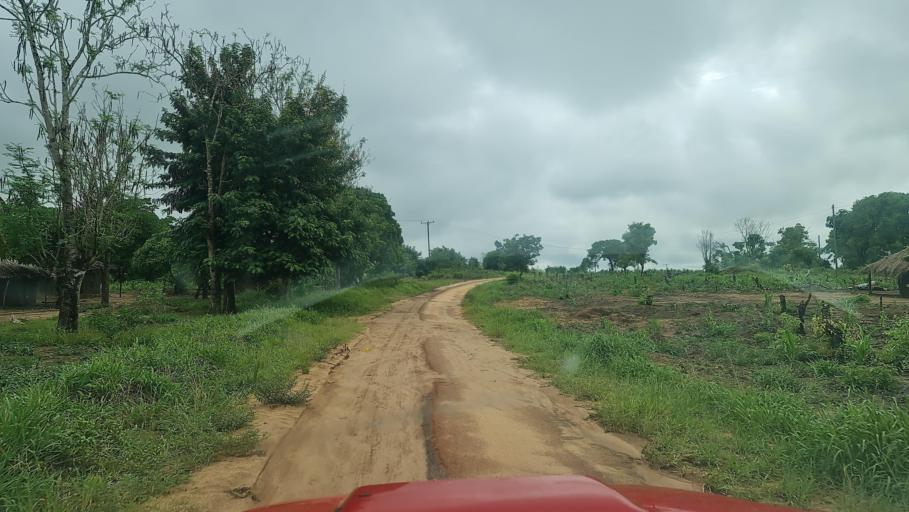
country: MW
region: Southern Region
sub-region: Nsanje District
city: Nsanje
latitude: -17.1781
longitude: 35.9002
